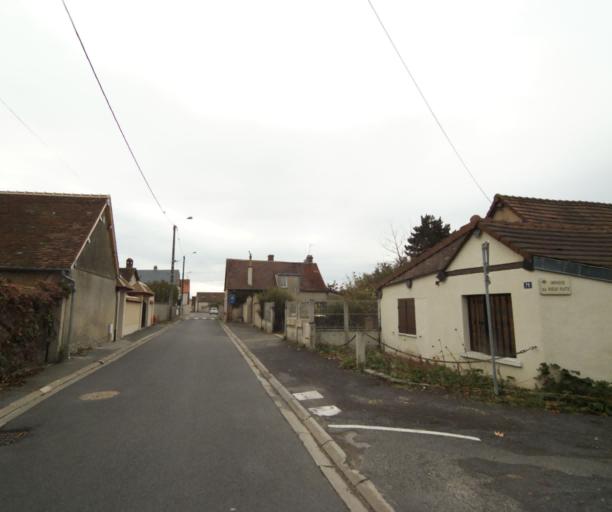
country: FR
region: Centre
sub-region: Departement d'Eure-et-Loir
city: Dreux
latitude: 48.7558
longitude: 1.3357
